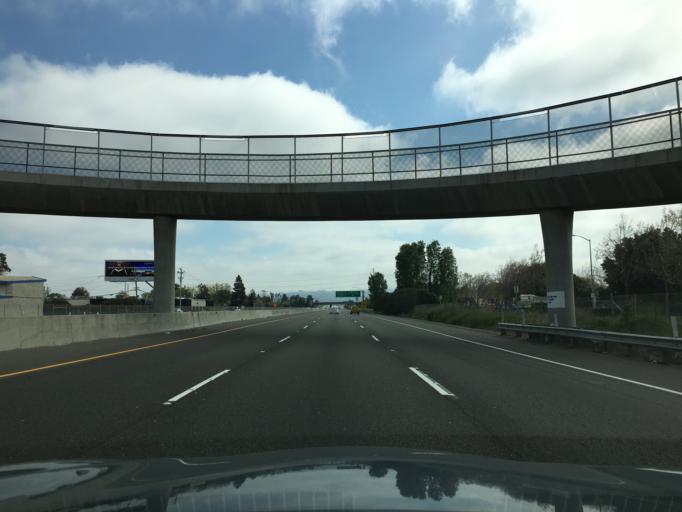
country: US
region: California
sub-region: Alameda County
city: San Lorenzo
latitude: 37.6256
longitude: -122.1287
